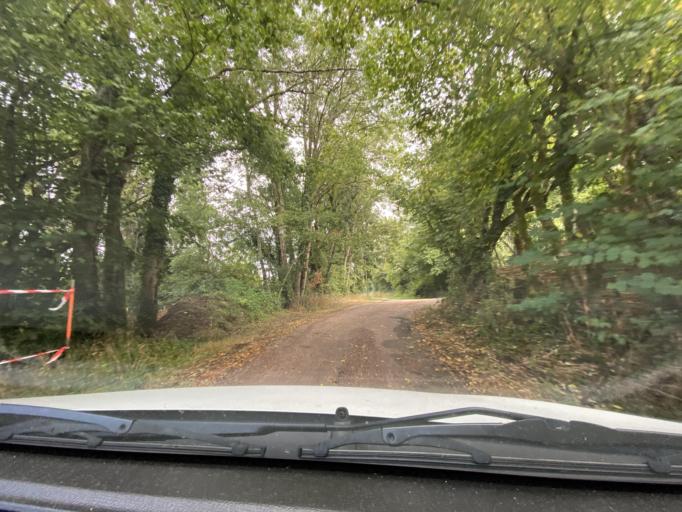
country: FR
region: Bourgogne
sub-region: Departement de la Cote-d'Or
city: Saulieu
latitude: 47.2798
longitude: 4.2410
